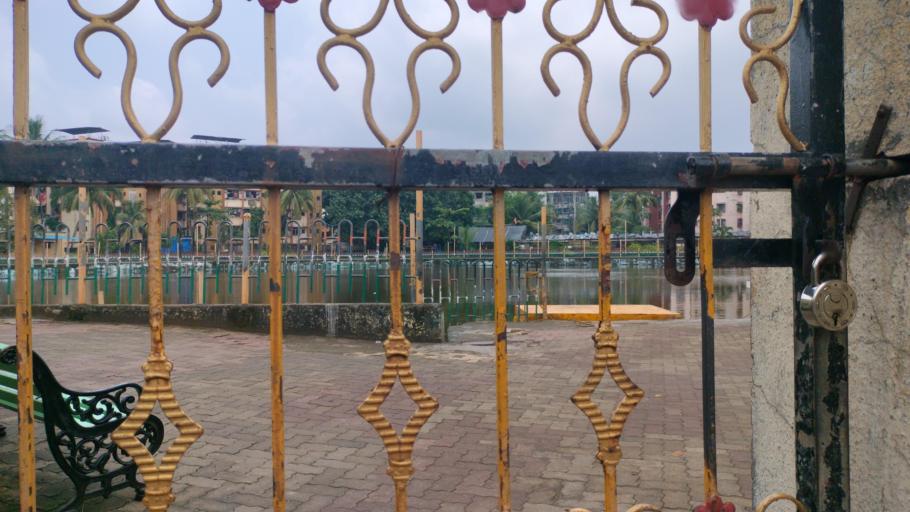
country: IN
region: Maharashtra
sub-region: Thane
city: Virar
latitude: 19.4159
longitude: 72.8280
